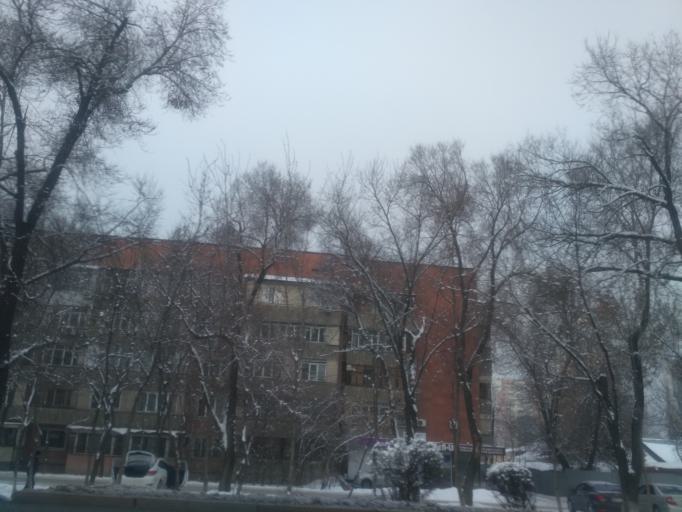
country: KZ
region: Almaty Qalasy
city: Almaty
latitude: 43.2221
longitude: 76.9350
